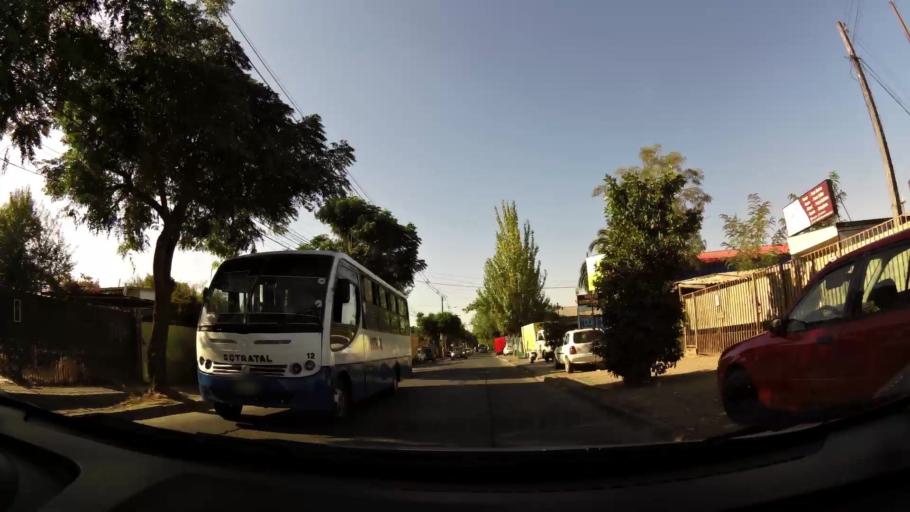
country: CL
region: Maule
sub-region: Provincia de Talca
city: Talca
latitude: -35.4418
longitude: -71.6667
